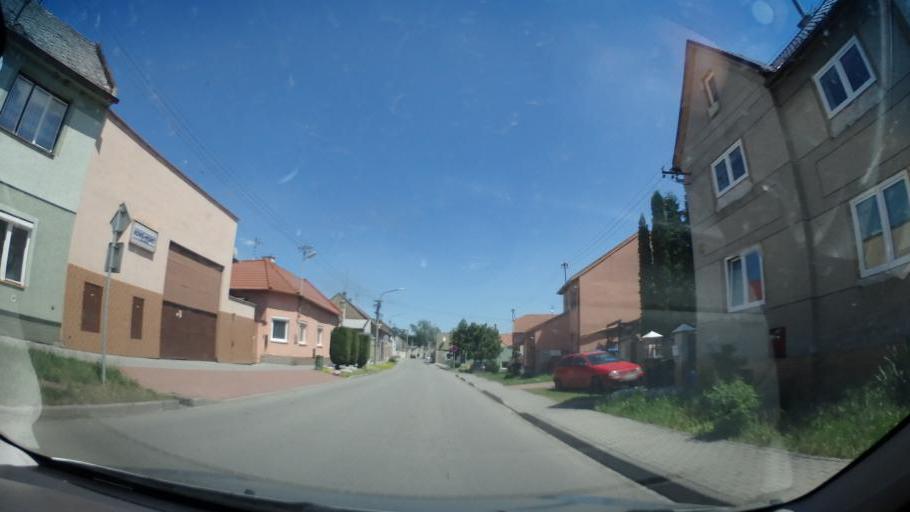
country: CZ
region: Olomoucky
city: Nemcice nad Hanou
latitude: 49.3412
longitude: 17.2462
